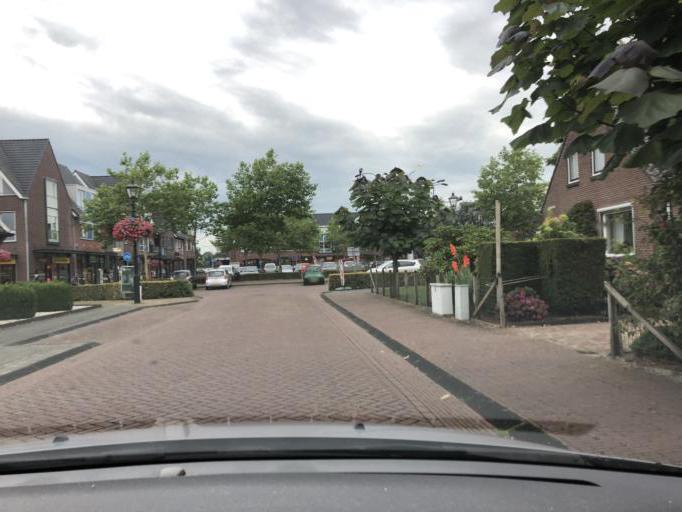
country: NL
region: Overijssel
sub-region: Gemeente Dalfsen
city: Dalfsen
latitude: 52.5740
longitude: 6.2926
